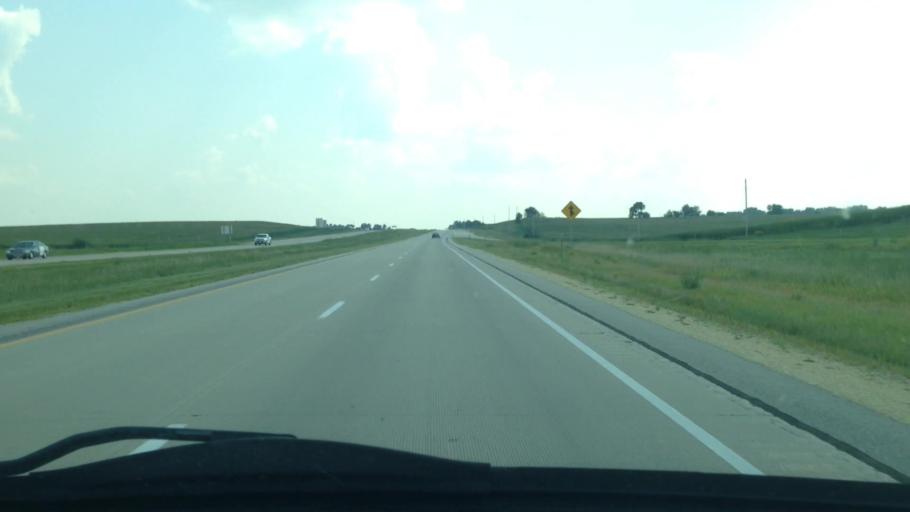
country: US
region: Iowa
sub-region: Bremer County
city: Denver
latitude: 42.7129
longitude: -92.3375
